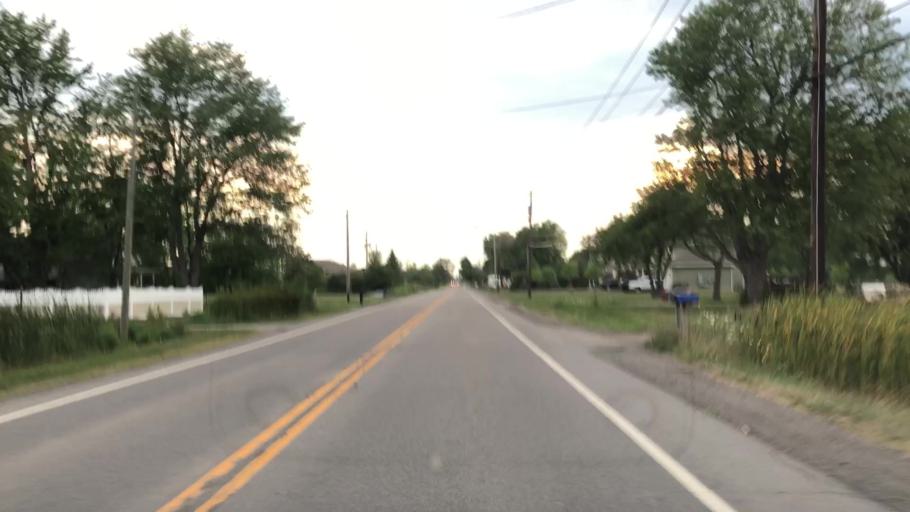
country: US
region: New York
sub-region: Erie County
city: Elma Center
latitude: 42.8390
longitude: -78.6727
